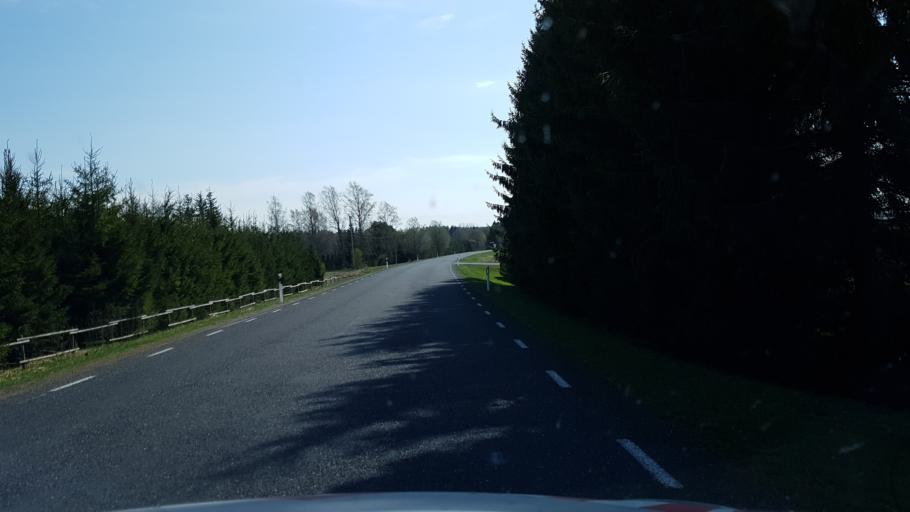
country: EE
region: Harju
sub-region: Keila linn
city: Keila
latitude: 59.4019
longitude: 24.4115
